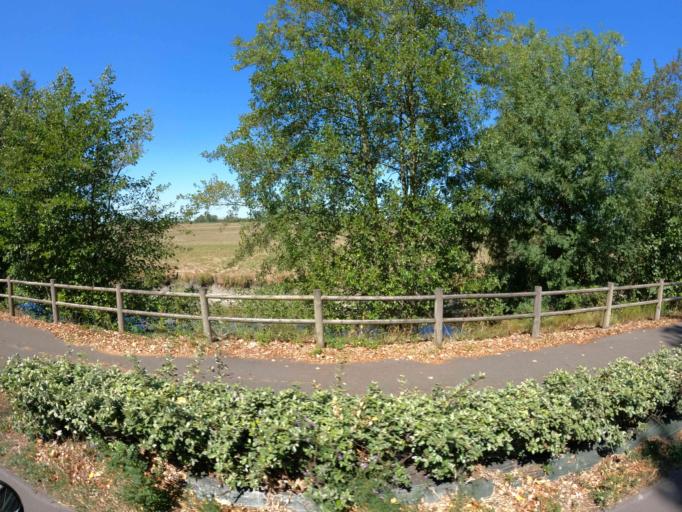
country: FR
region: Pays de la Loire
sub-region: Departement de la Vendee
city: Sallertaine
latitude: 46.8260
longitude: -1.9561
